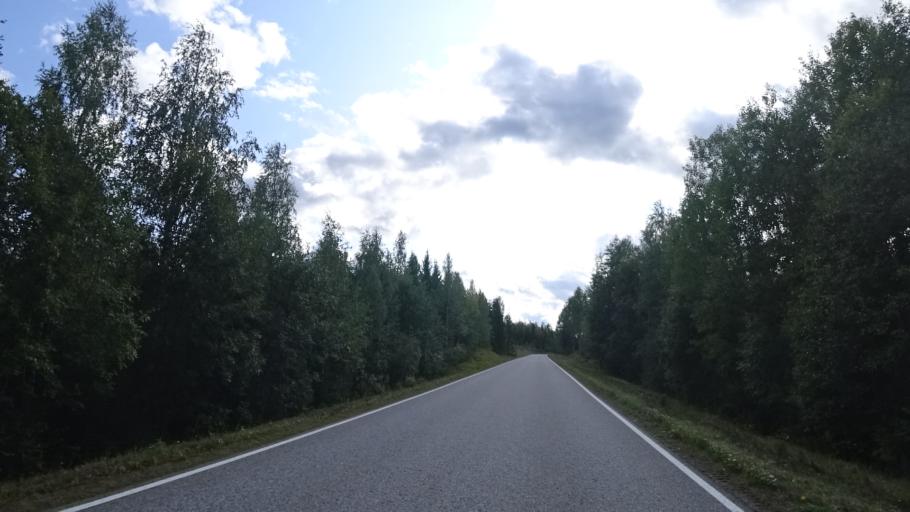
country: RU
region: Republic of Karelia
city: Vyartsilya
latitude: 62.2265
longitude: 30.6612
